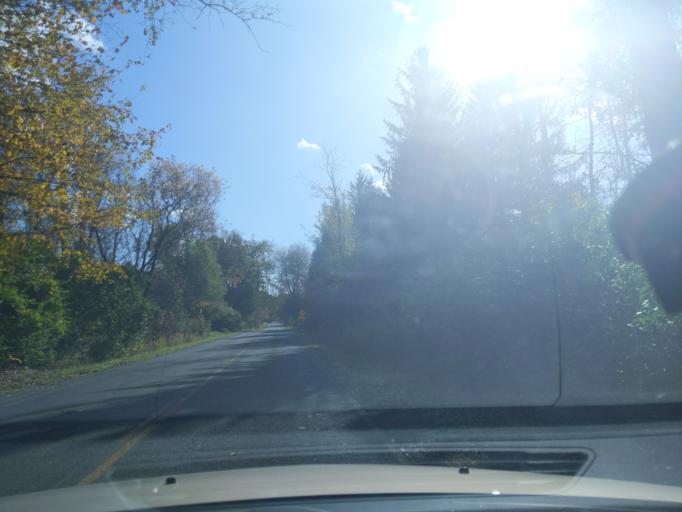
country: US
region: Michigan
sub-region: Ingham County
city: Haslett
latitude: 42.7358
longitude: -84.3931
